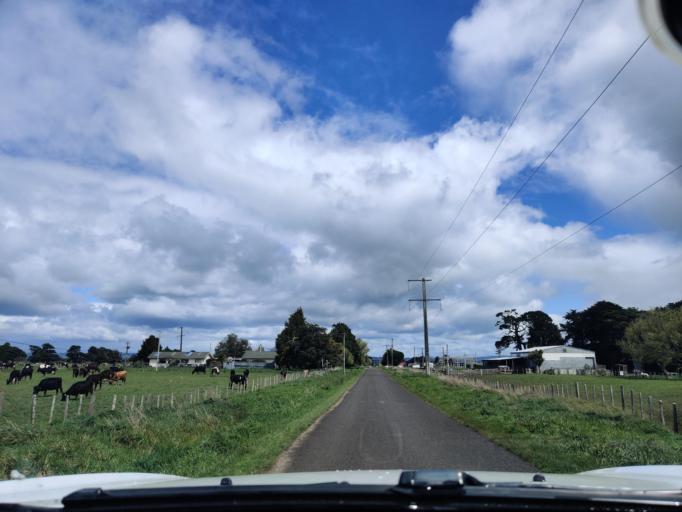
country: NZ
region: Manawatu-Wanganui
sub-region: Palmerston North City
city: Palmerston North
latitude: -40.3117
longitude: 175.8583
